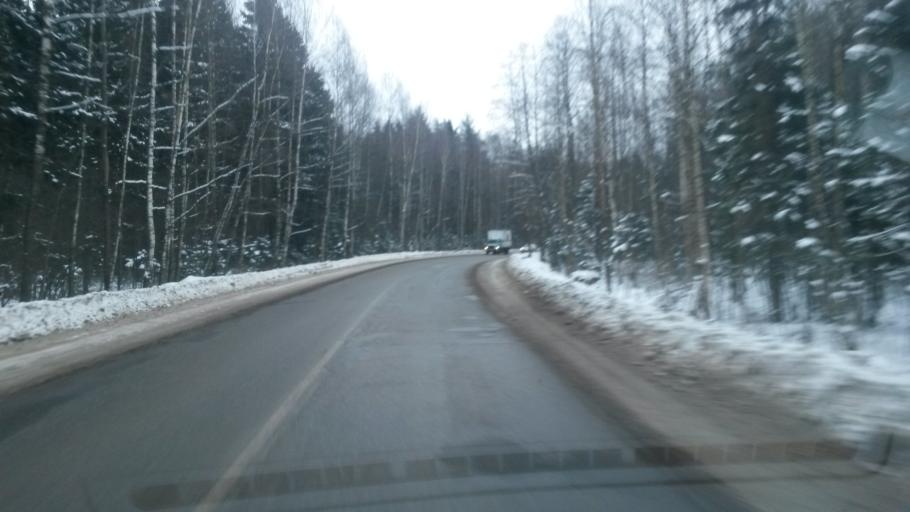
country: RU
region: Ivanovo
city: Kokhma
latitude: 56.9692
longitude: 41.0898
